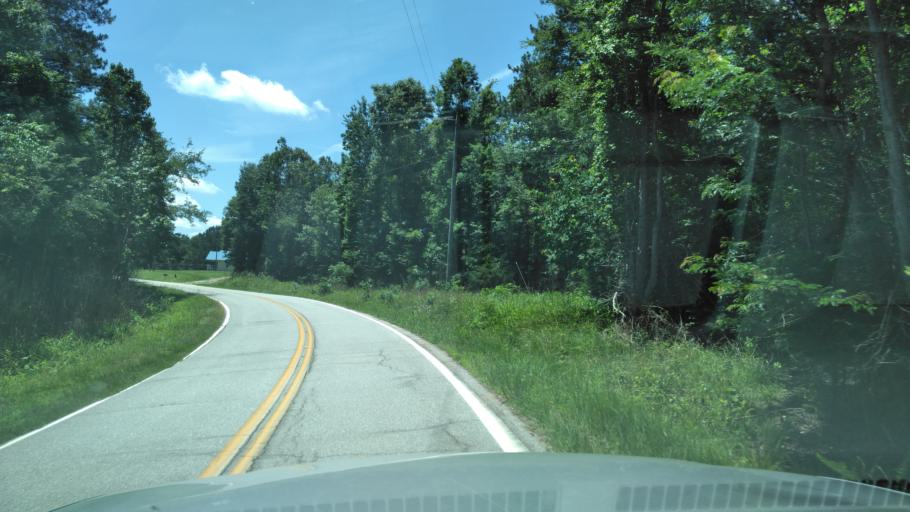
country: US
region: South Carolina
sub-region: Laurens County
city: Laurens
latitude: 34.3817
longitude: -82.0894
